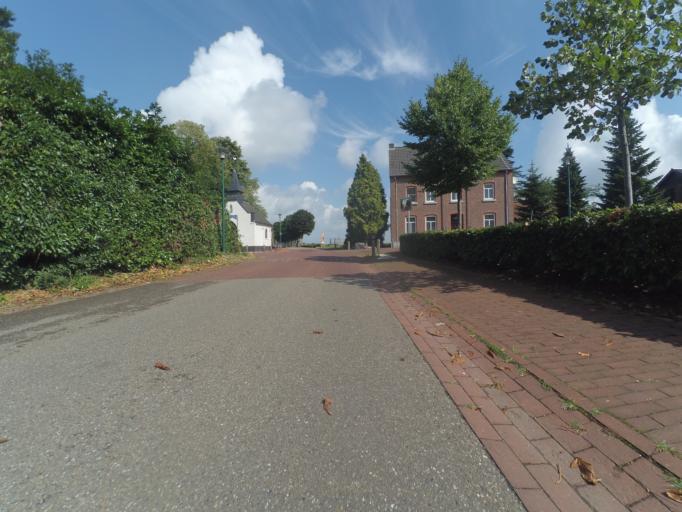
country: NL
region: Limburg
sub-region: Gemeente Echt-Susteren
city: Koningsbosch
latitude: 51.0358
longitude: 5.9573
